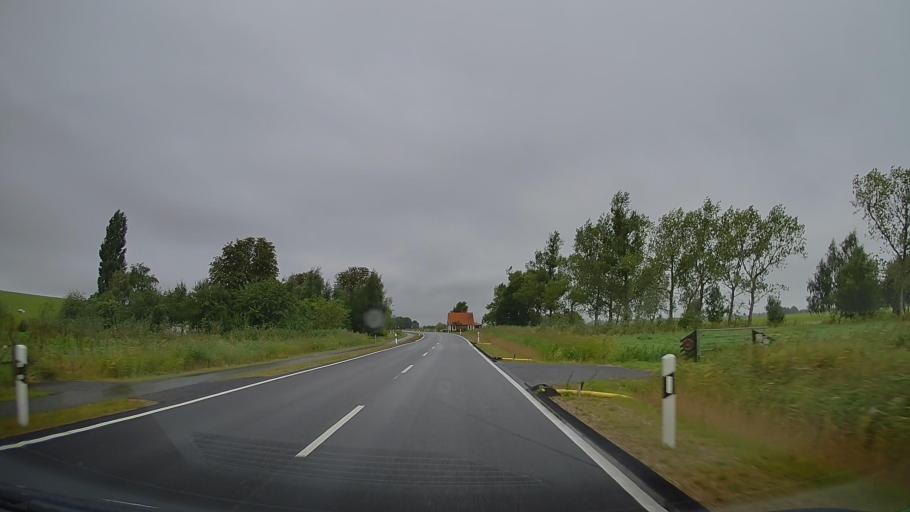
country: DE
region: Schleswig-Holstein
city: Brokdorf
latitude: 53.8700
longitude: 9.3054
